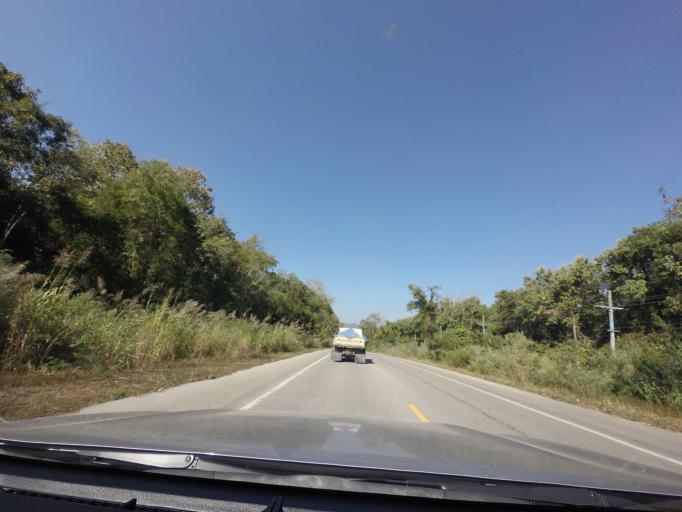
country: TH
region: Lampang
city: Mae Mo
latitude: 18.4978
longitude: 99.6472
